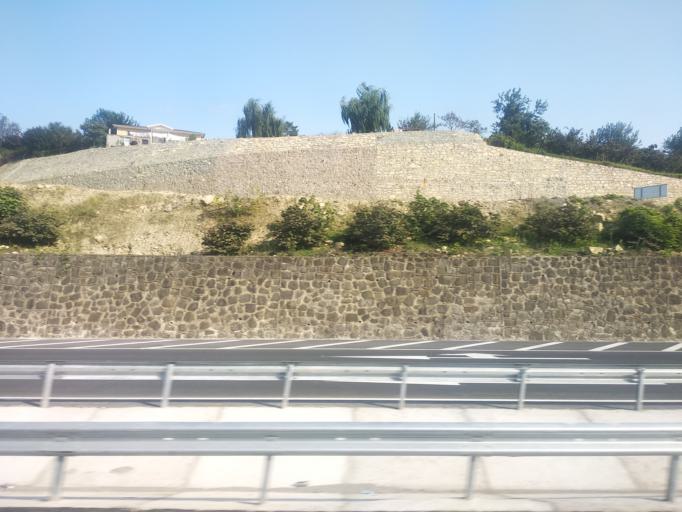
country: TR
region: Ordu
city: Ordu
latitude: 40.9928
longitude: 37.8160
